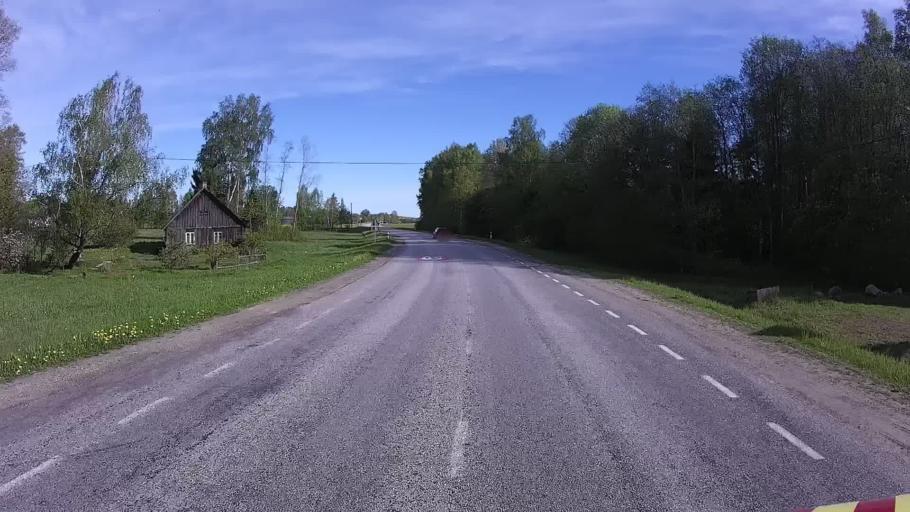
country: EE
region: Tartu
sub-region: Elva linn
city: Elva
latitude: 58.1310
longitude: 26.5227
